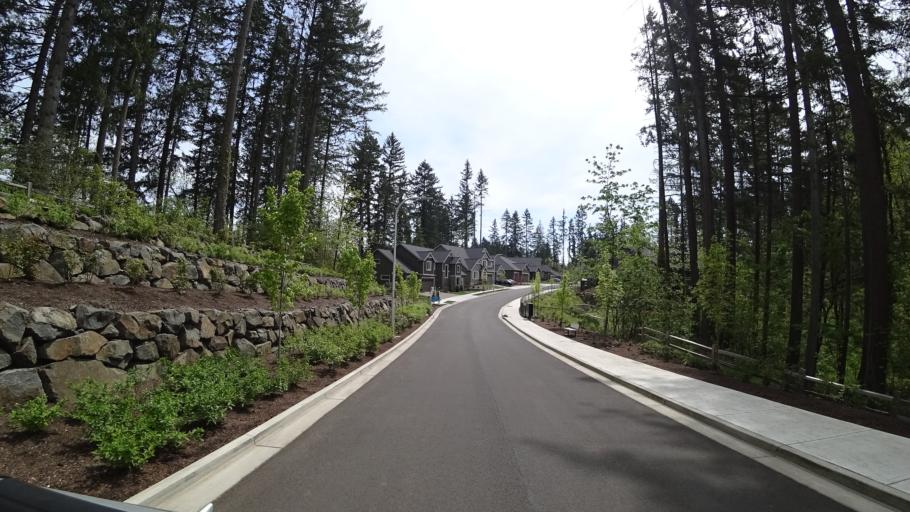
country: US
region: Oregon
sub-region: Washington County
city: Hillsboro
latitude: 45.5081
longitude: -122.9402
